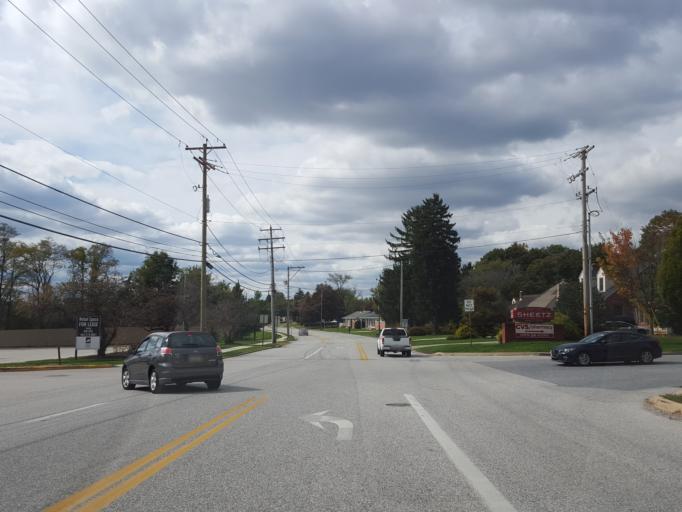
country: US
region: Pennsylvania
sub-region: York County
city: Valley View
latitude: 39.9355
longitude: -76.6932
